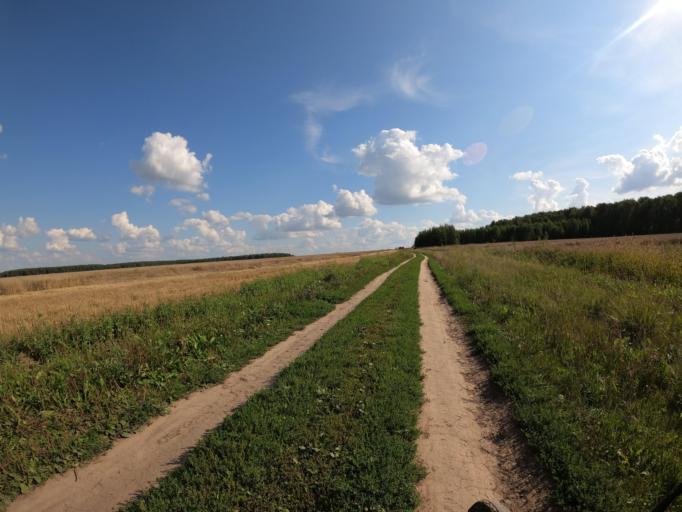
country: RU
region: Moskovskaya
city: Troitskoye
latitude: 55.2283
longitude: 38.4856
